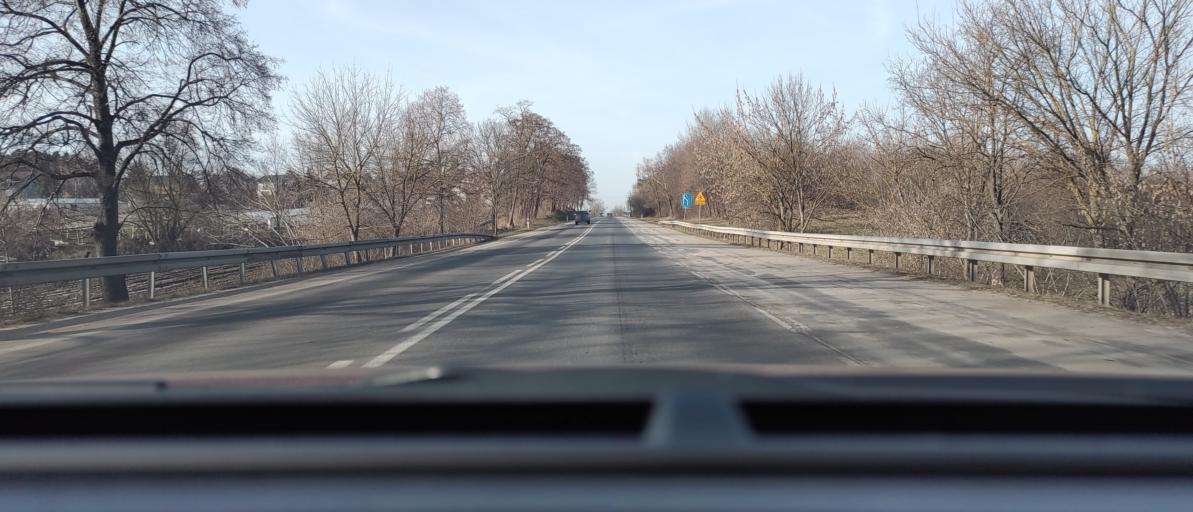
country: PL
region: Masovian Voivodeship
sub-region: Powiat bialobrzeski
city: Promna
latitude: 51.6702
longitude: 20.9452
